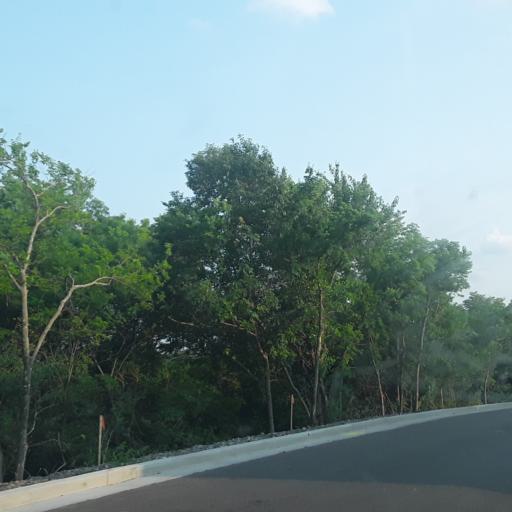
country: US
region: Tennessee
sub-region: Williamson County
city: Brentwood Estates
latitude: 36.0420
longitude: -86.7205
